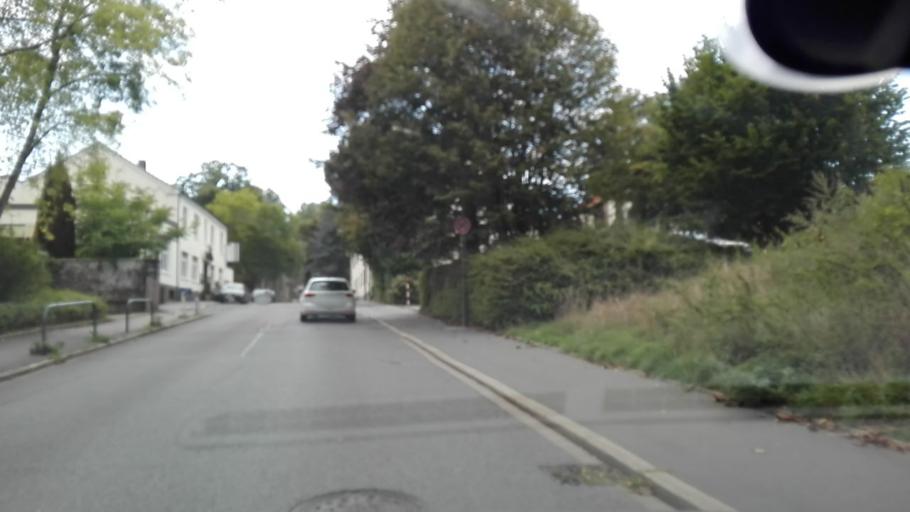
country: DE
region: North Rhine-Westphalia
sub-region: Regierungsbezirk Arnsberg
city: Dortmund
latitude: 51.4906
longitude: 7.4316
